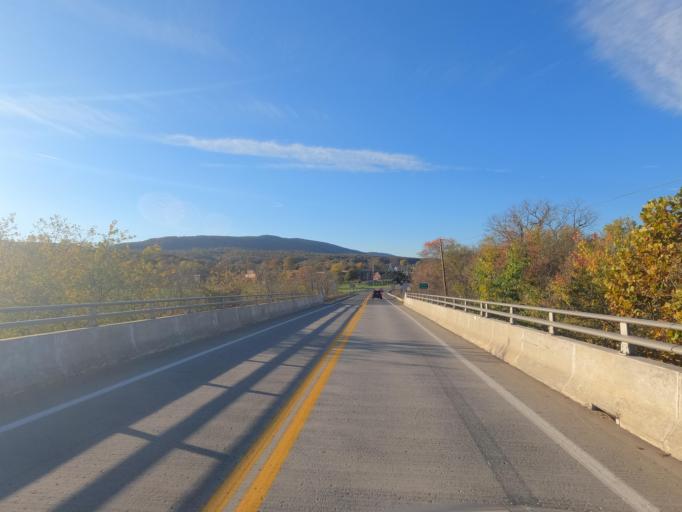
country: US
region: West Virginia
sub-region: Morgan County
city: Berkeley Springs
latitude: 39.5384
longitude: -78.4556
